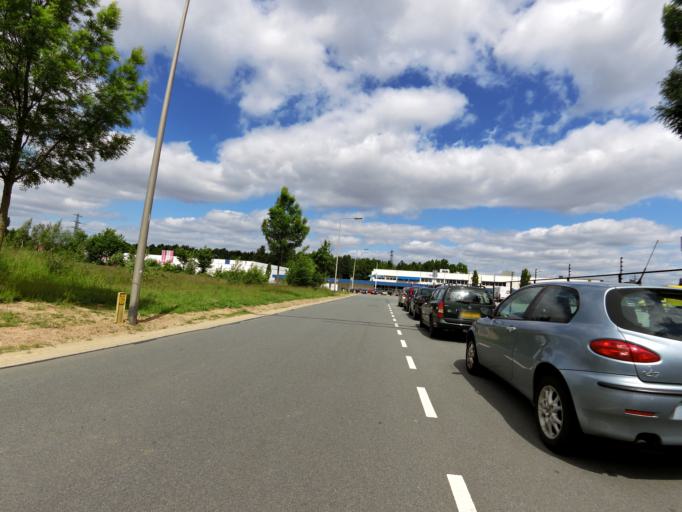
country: NL
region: Limburg
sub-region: Gemeente Heerlen
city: Heerlen
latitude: 50.8597
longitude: 6.0109
